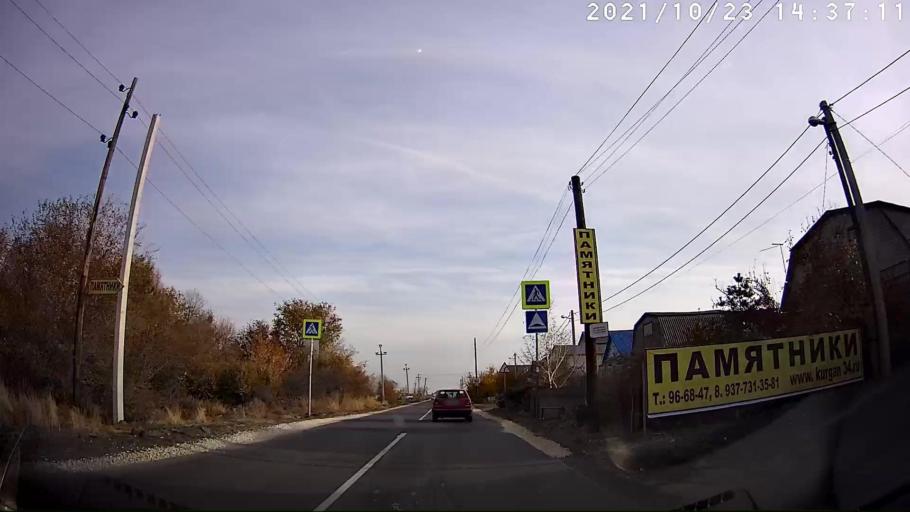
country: RU
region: Volgograd
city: Krasnoslobodsk
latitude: 48.4989
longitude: 44.5471
